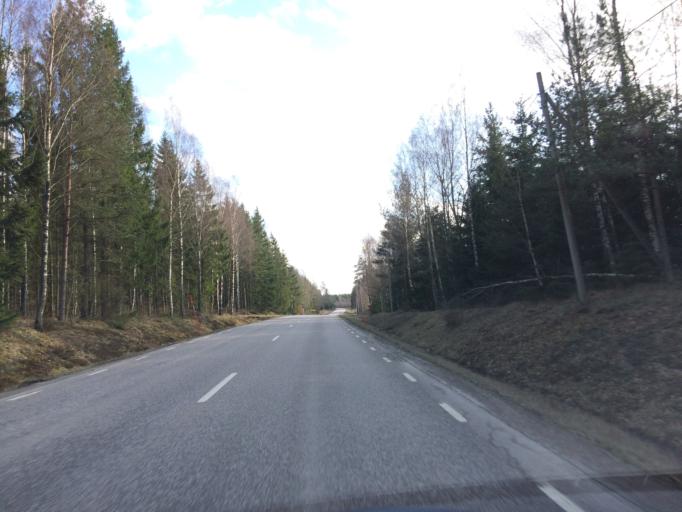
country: SE
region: Kronoberg
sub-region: Almhults Kommun
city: AElmhult
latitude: 56.5878
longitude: 14.0980
